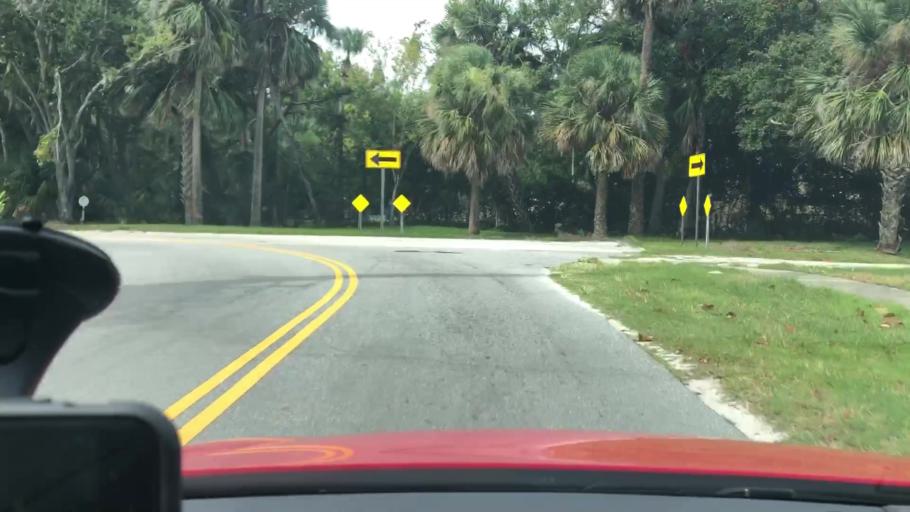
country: US
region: Florida
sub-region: Volusia County
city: South Daytona
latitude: 29.1842
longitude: -81.0068
